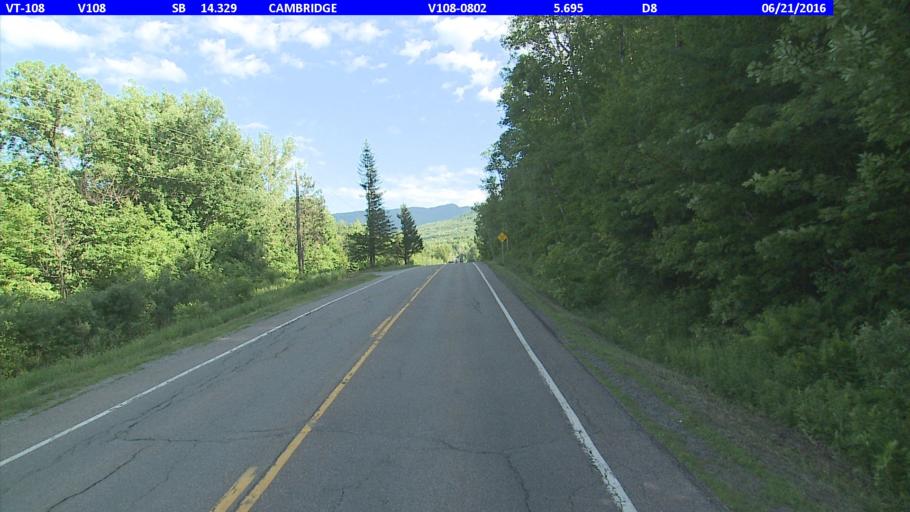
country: US
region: Vermont
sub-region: Lamoille County
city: Johnson
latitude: 44.6067
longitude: -72.8108
